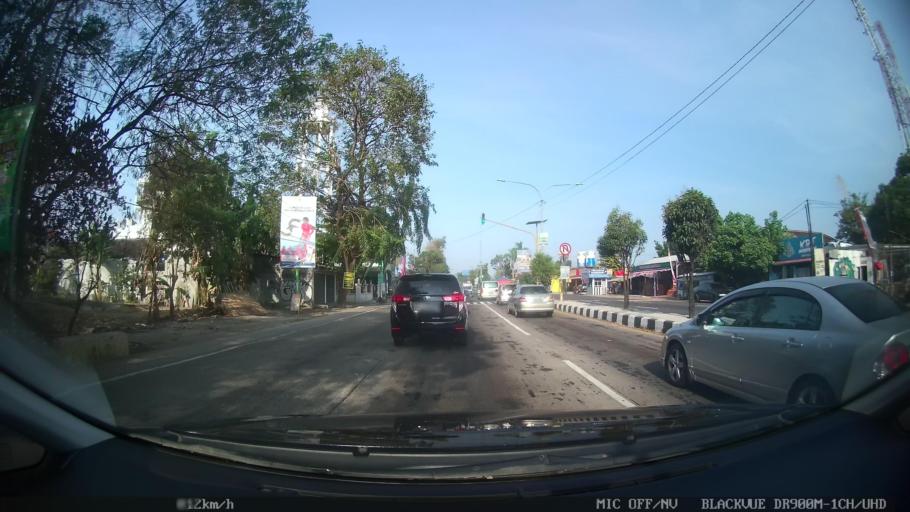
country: ID
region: Daerah Istimewa Yogyakarta
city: Kasihan
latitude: -7.8263
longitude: 110.3445
